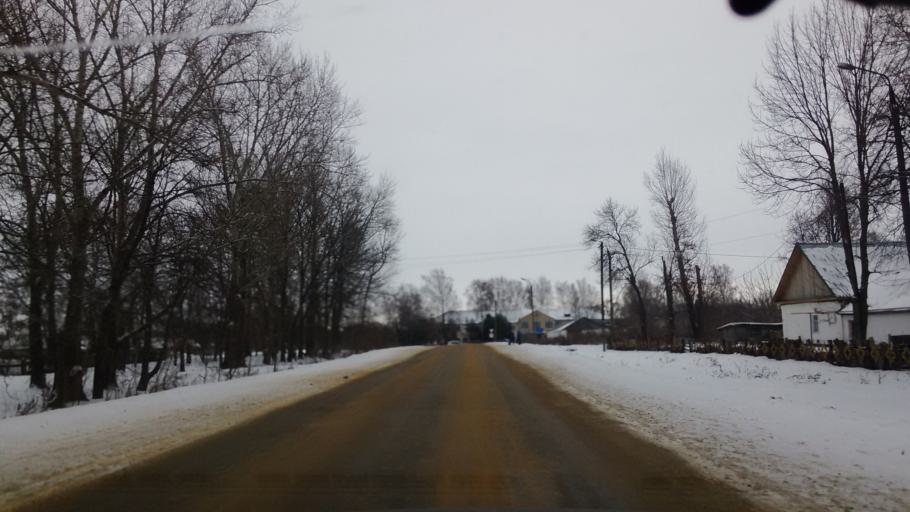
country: RU
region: Tula
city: Bogoroditsk
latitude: 53.7613
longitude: 37.9904
